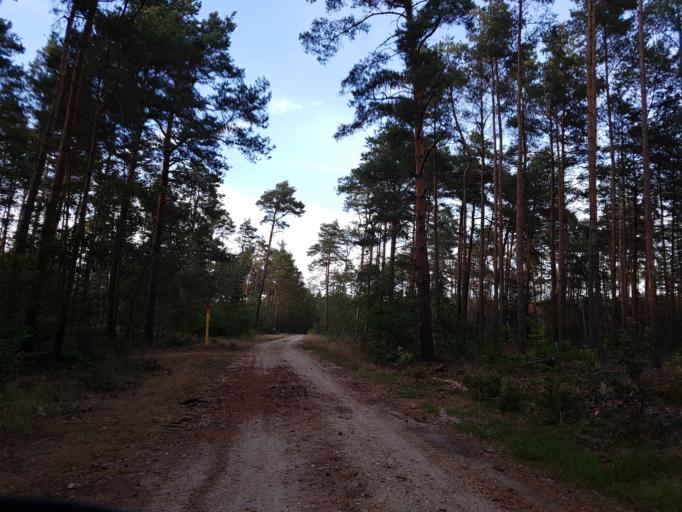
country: DE
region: Brandenburg
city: Trobitz
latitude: 51.5572
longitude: 13.4502
